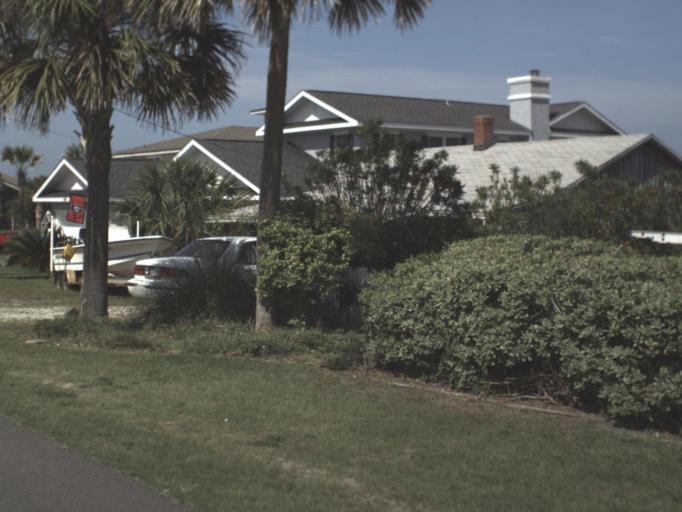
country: US
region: Florida
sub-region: Nassau County
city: Fernandina Beach
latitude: 30.6248
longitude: -81.4400
